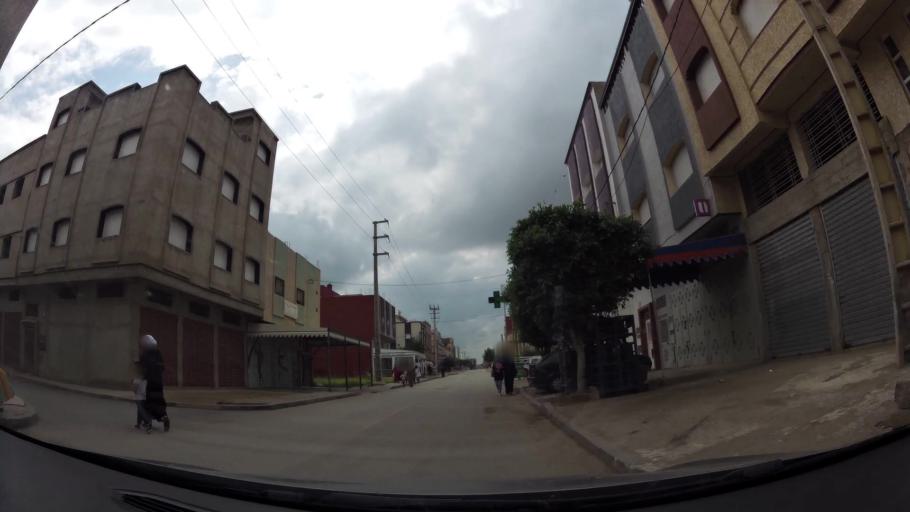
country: MA
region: Rabat-Sale-Zemmour-Zaer
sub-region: Khemisset
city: Tiflet
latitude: 33.8883
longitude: -6.3194
